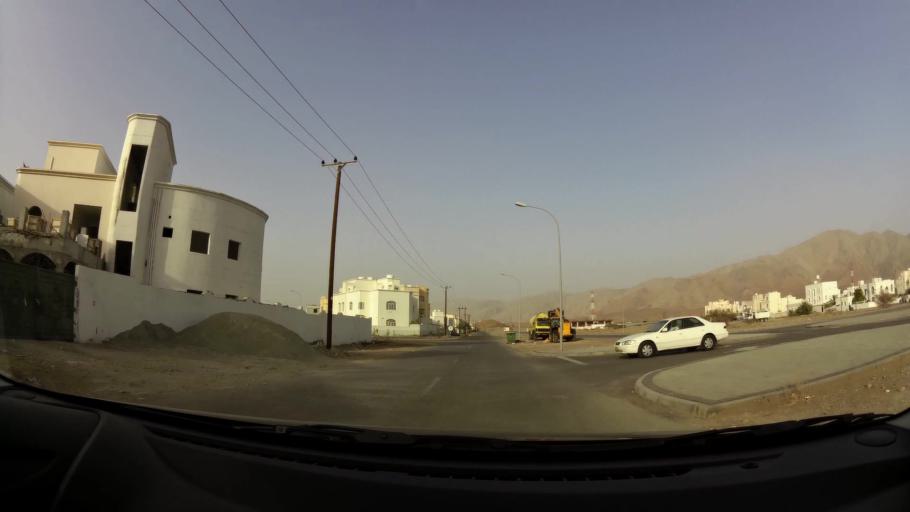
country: OM
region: Muhafazat Masqat
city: Bawshar
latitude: 23.5309
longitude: 58.3485
